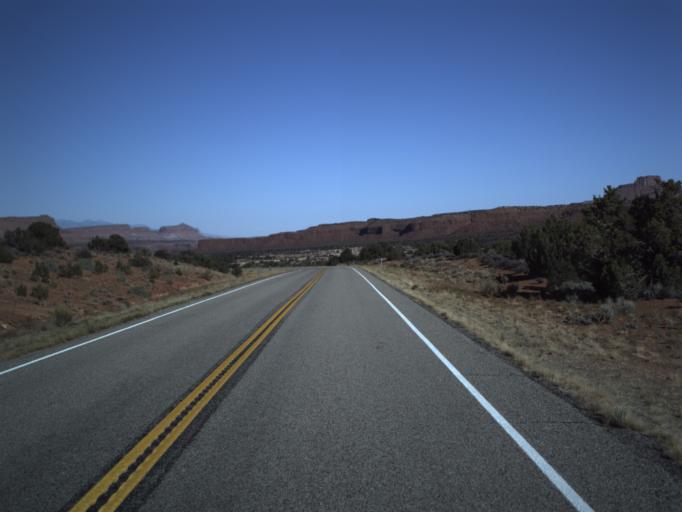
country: US
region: Utah
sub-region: San Juan County
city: Blanding
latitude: 37.6537
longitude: -110.1729
